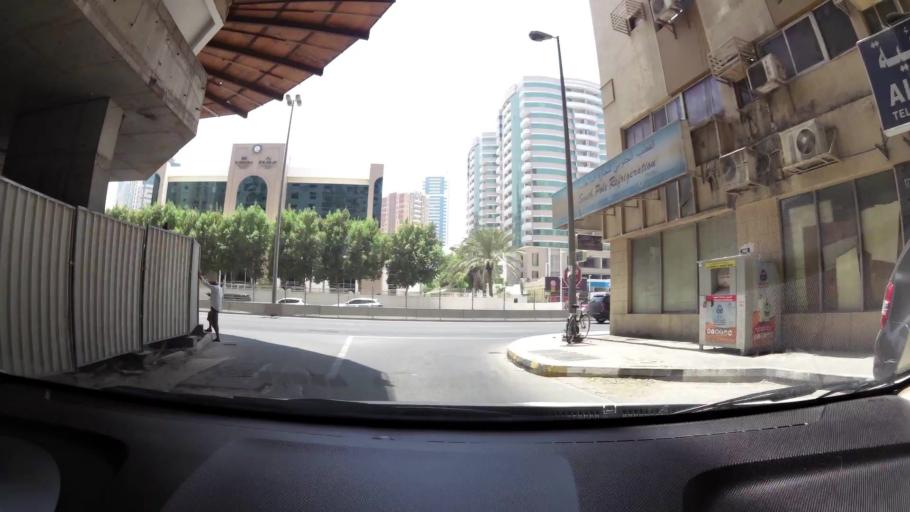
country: AE
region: Ash Shariqah
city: Sharjah
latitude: 25.3170
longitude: 55.3806
